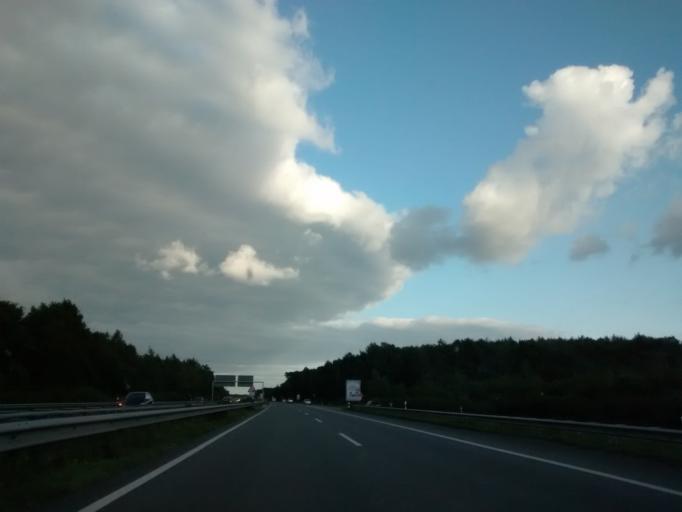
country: DE
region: Lower Saxony
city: Schuttorf
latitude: 52.3407
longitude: 7.2633
